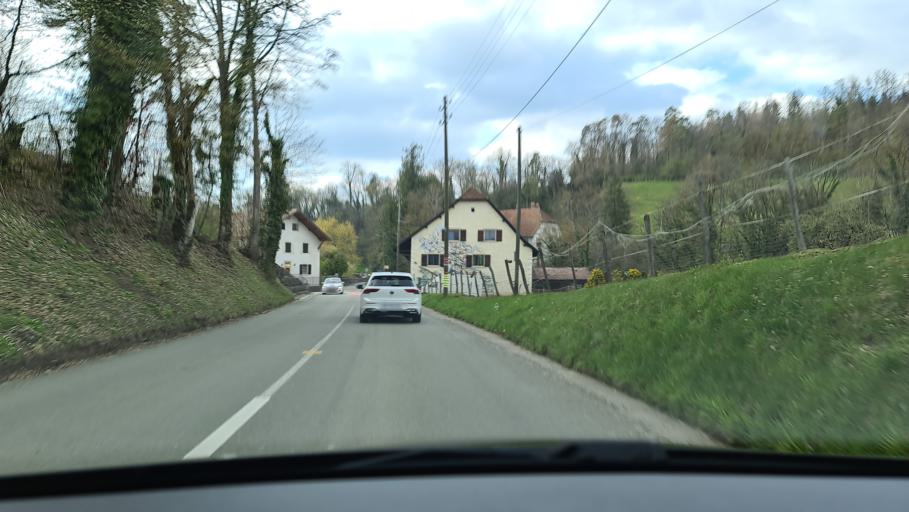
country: CH
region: Jura
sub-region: Porrentruy District
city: Boncourt
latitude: 47.4701
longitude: 7.0480
